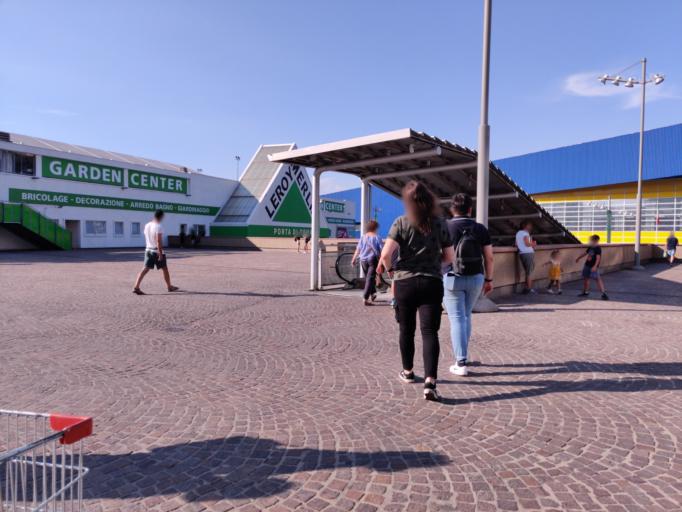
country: IT
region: Latium
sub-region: Citta metropolitana di Roma Capitale
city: Colle Verde
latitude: 41.9720
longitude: 12.5407
